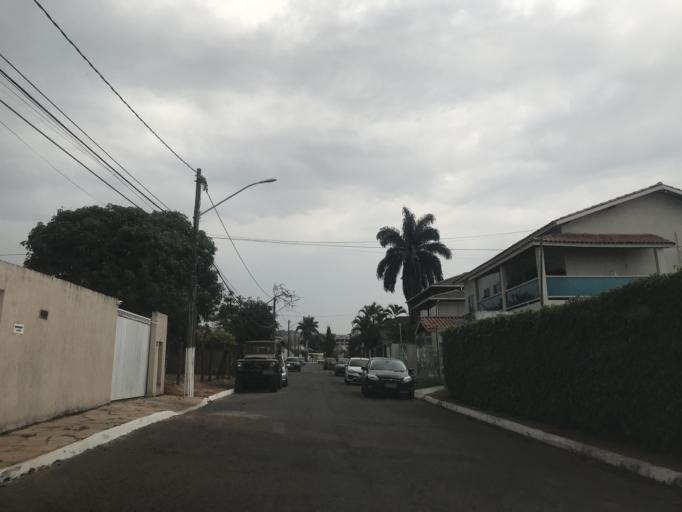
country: BR
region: Federal District
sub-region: Brasilia
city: Brasilia
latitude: -15.6632
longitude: -47.8315
